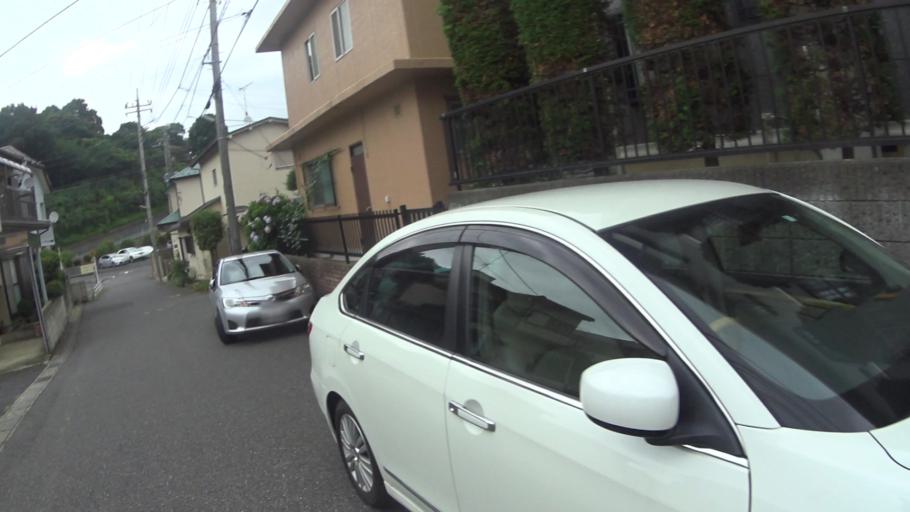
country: JP
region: Chiba
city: Nagareyama
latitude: 35.8352
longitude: 139.9217
